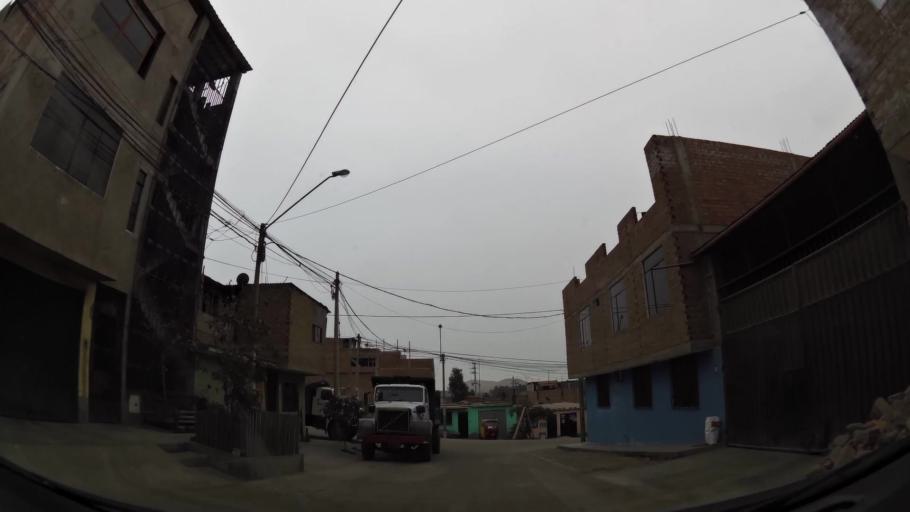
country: PE
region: Lima
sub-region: Lima
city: Surco
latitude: -12.1861
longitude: -76.9833
